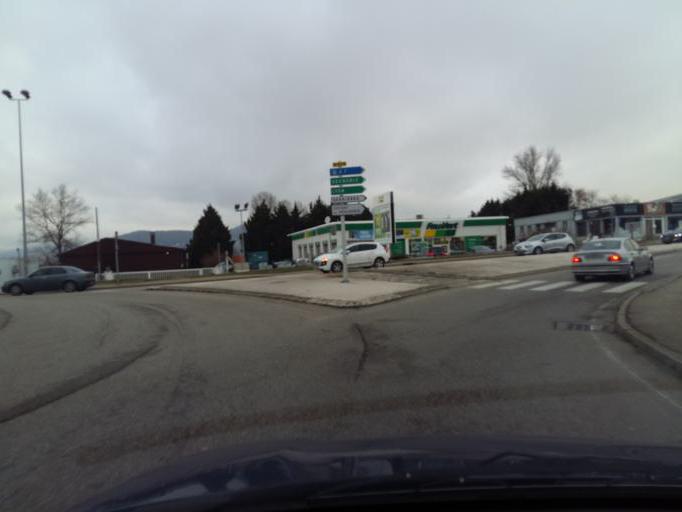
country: FR
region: Rhone-Alpes
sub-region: Departement de l'Ardeche
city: Davezieux
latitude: 45.2560
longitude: 4.6958
